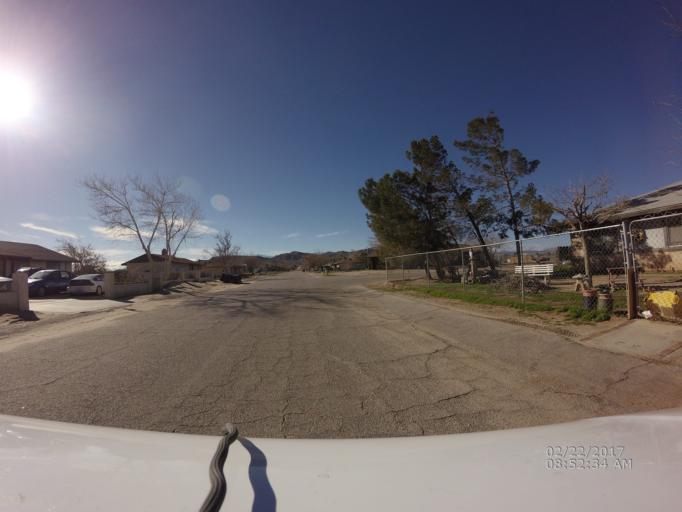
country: US
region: California
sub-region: Los Angeles County
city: Lake Los Angeles
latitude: 34.6277
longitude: -117.8522
